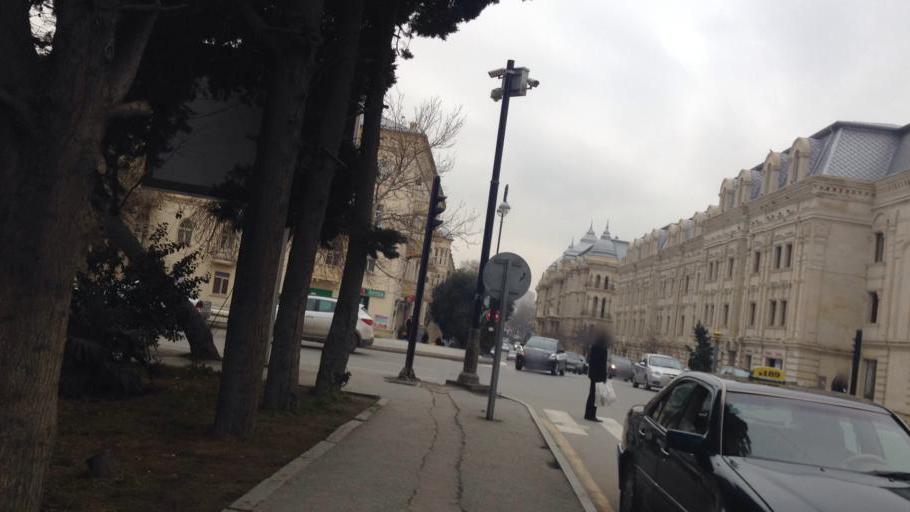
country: AZ
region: Baki
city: Baku
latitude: 40.3904
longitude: 49.8427
